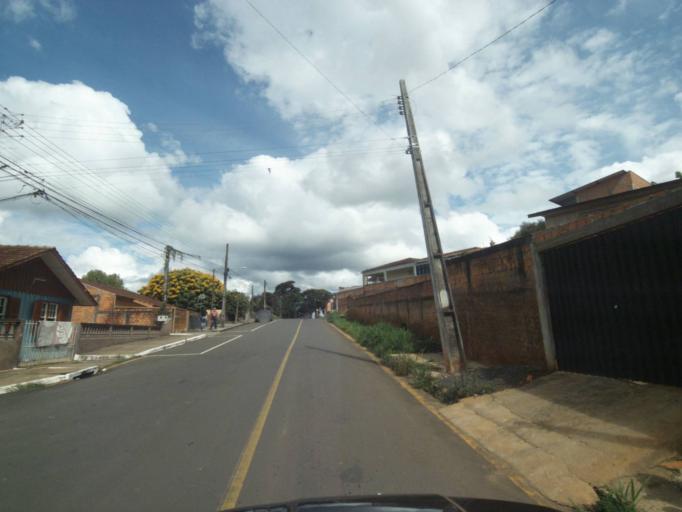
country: BR
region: Parana
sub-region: Telemaco Borba
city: Telemaco Borba
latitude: -24.3218
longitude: -50.6273
